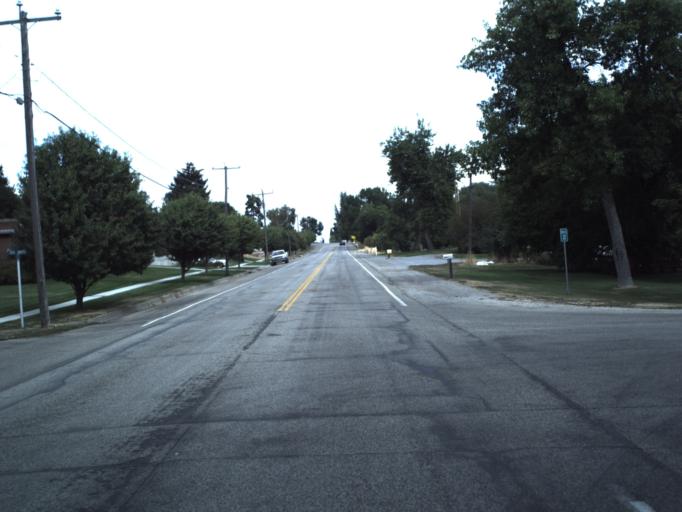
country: US
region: Utah
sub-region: Cache County
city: Wellsville
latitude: 41.6449
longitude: -111.9342
